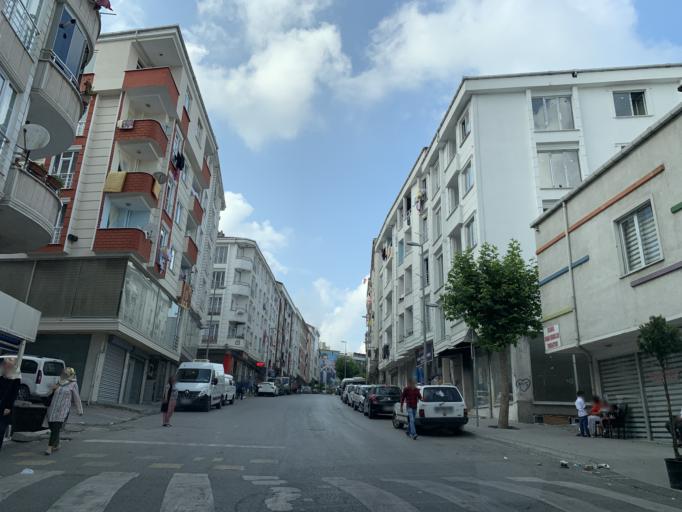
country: TR
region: Istanbul
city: Esenyurt
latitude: 41.0301
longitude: 28.6747
